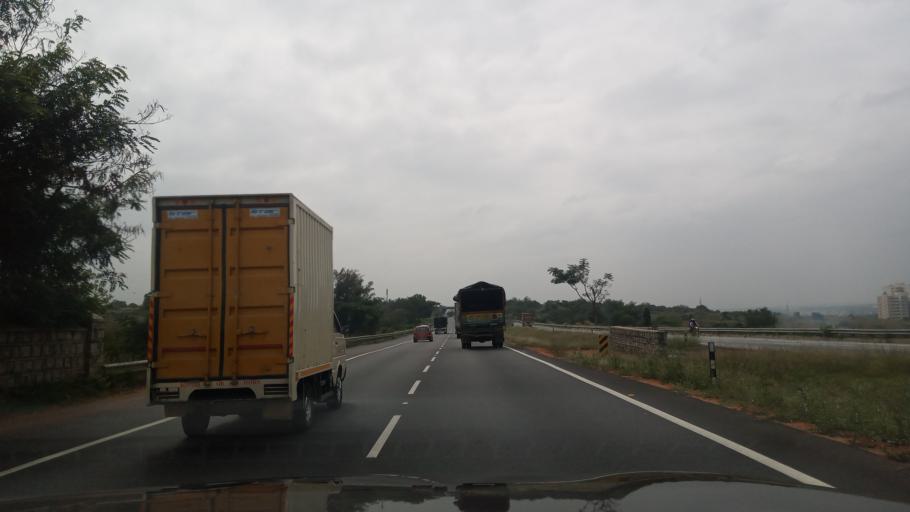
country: IN
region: Karnataka
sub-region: Bangalore Urban
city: Bangalore
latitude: 12.9197
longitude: 77.4689
